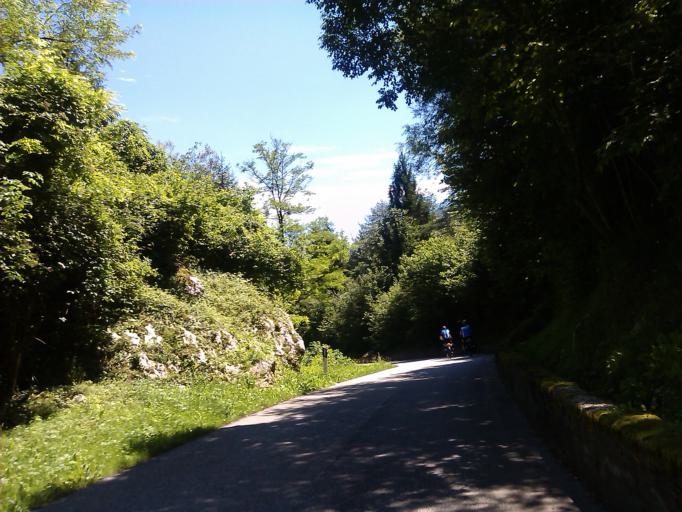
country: IT
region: Veneto
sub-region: Provincia di Vicenza
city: Enego
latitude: 45.9797
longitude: 11.6733
